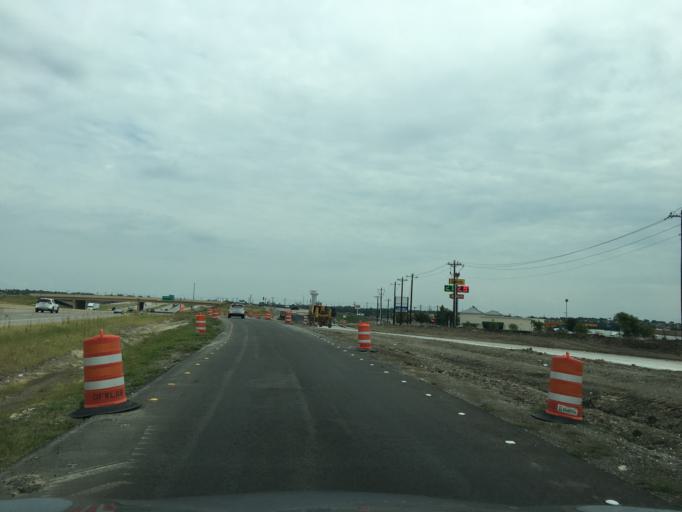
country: US
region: Texas
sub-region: Collin County
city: Anna
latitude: 33.3424
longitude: -96.5868
